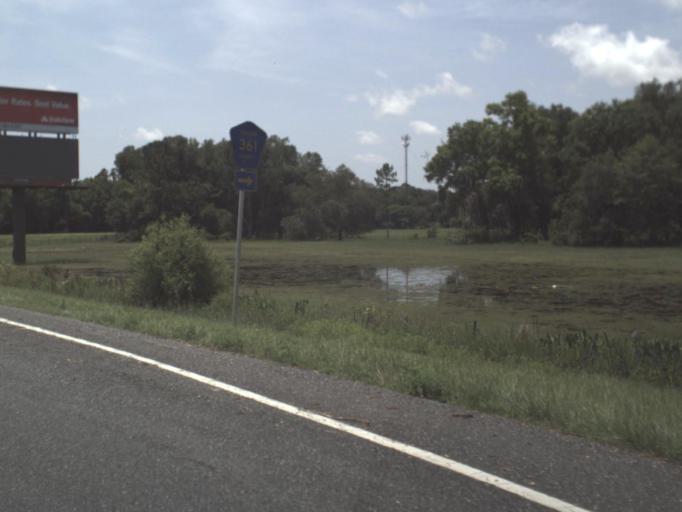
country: US
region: Florida
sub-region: Taylor County
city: Perry
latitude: 30.0526
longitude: -83.5521
